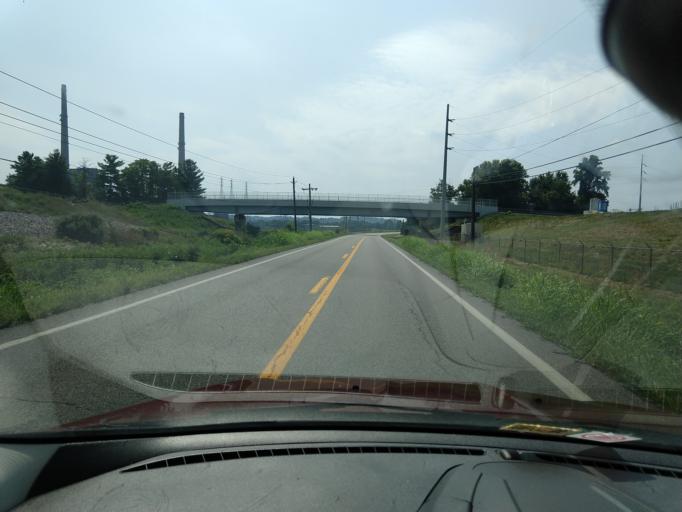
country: US
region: West Virginia
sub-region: Mason County
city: New Haven
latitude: 38.9701
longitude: -81.9320
